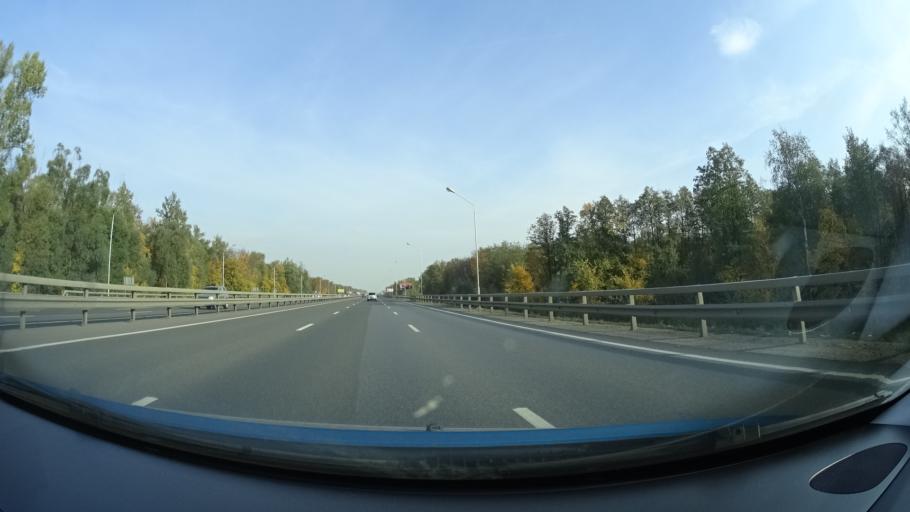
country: RU
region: Bashkortostan
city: Avdon
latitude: 54.6705
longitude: 55.8372
